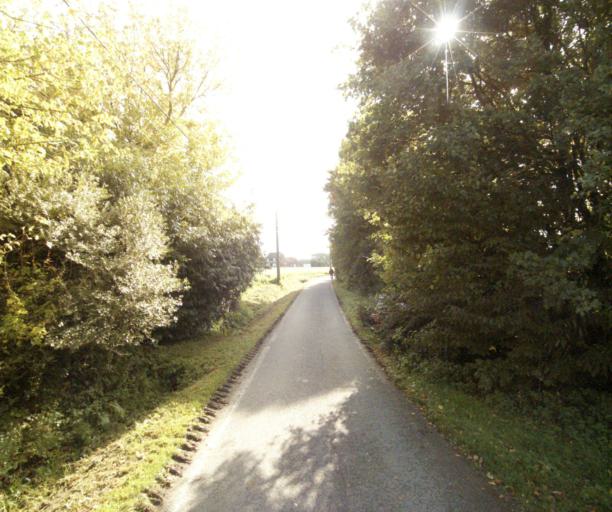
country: FR
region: Nord-Pas-de-Calais
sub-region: Departement du Nord
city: Verlinghem
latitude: 50.6781
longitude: 3.0037
